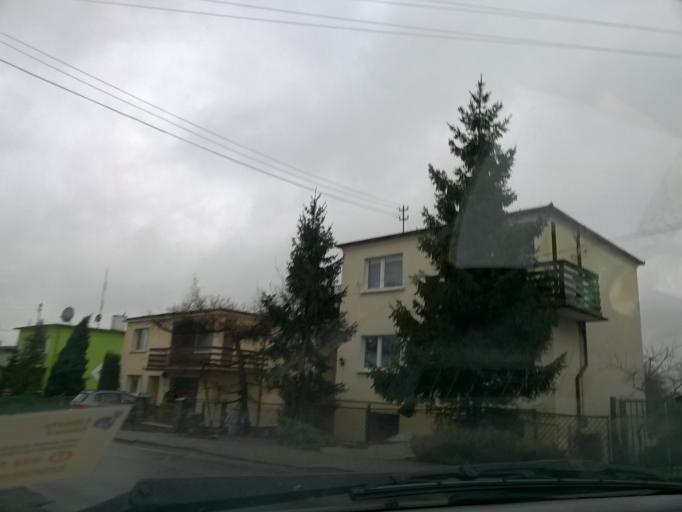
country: PL
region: Kujawsko-Pomorskie
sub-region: Powiat nakielski
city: Kcynia
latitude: 52.9939
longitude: 17.4828
